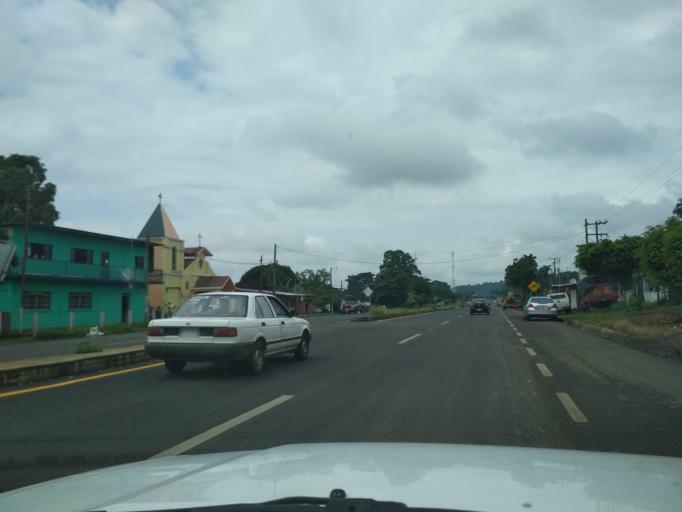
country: MX
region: Veracruz
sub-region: San Andres Tuxtla
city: Matacapan
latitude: 18.4347
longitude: -95.1643
